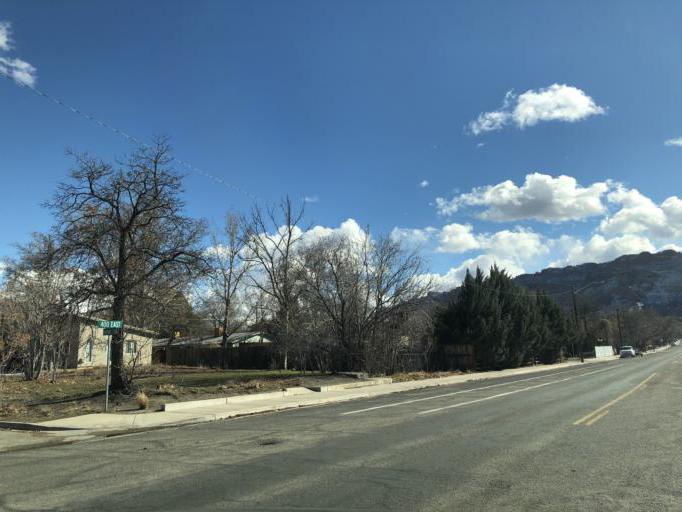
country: US
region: Utah
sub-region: Grand County
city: Moab
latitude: 38.5722
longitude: -109.5430
